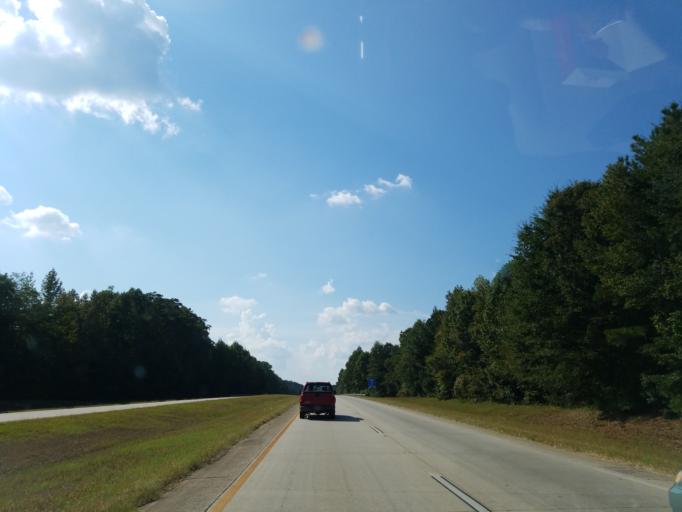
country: US
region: Georgia
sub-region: Oconee County
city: Bogart
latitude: 33.9187
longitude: -83.4904
